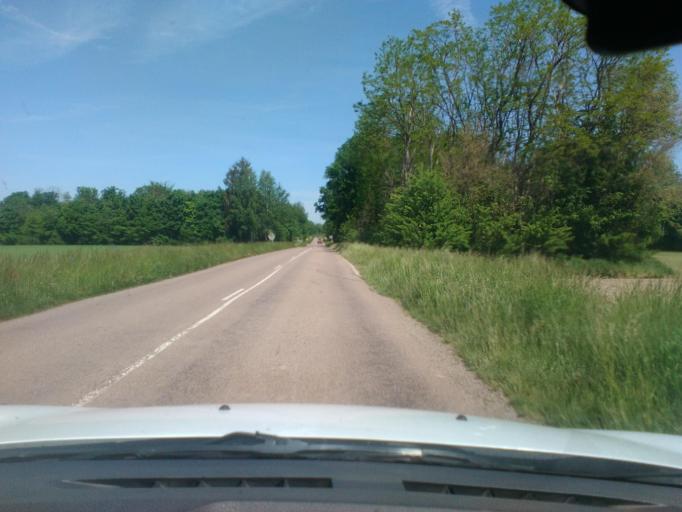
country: FR
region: Lorraine
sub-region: Departement des Vosges
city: Rambervillers
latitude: 48.4208
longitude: 6.5832
